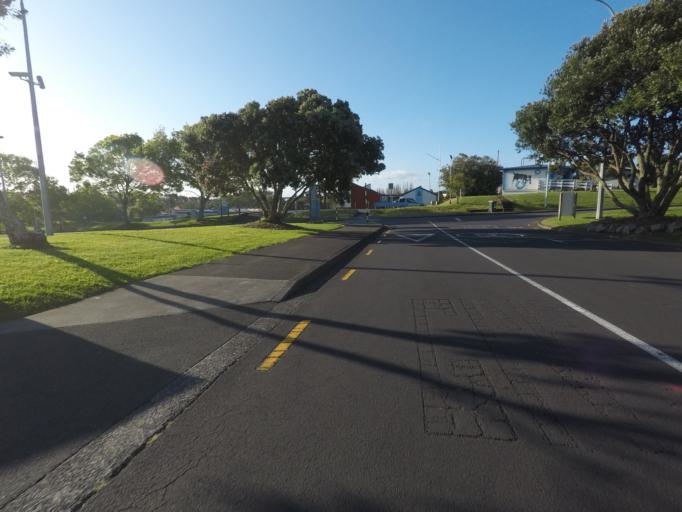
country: NZ
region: Auckland
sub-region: Auckland
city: Rosebank
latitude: -36.8784
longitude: 174.7096
